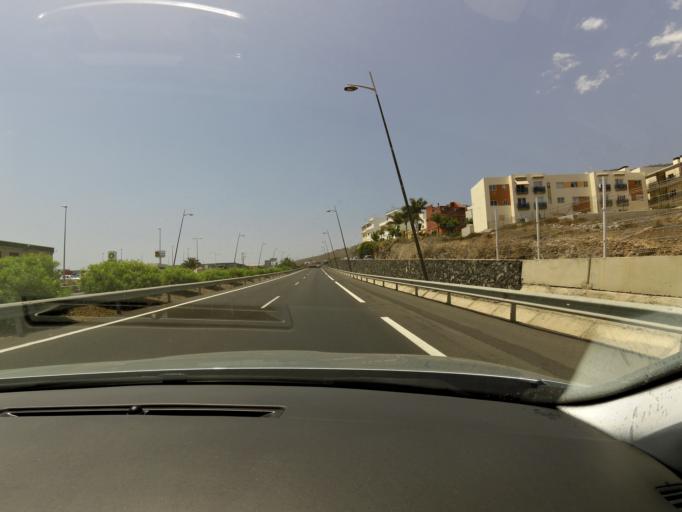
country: ES
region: Canary Islands
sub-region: Provincia de Santa Cruz de Tenerife
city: Adeje
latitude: 28.1181
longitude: -16.7376
